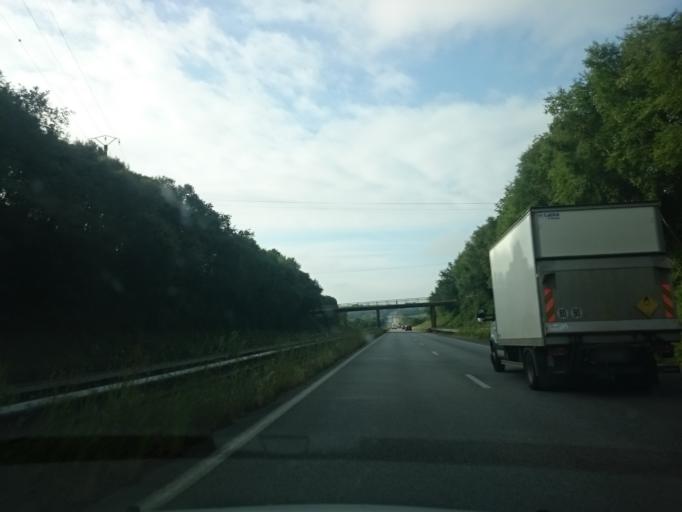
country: FR
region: Brittany
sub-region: Departement du Finistere
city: Briec
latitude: 48.1437
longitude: -4.0317
